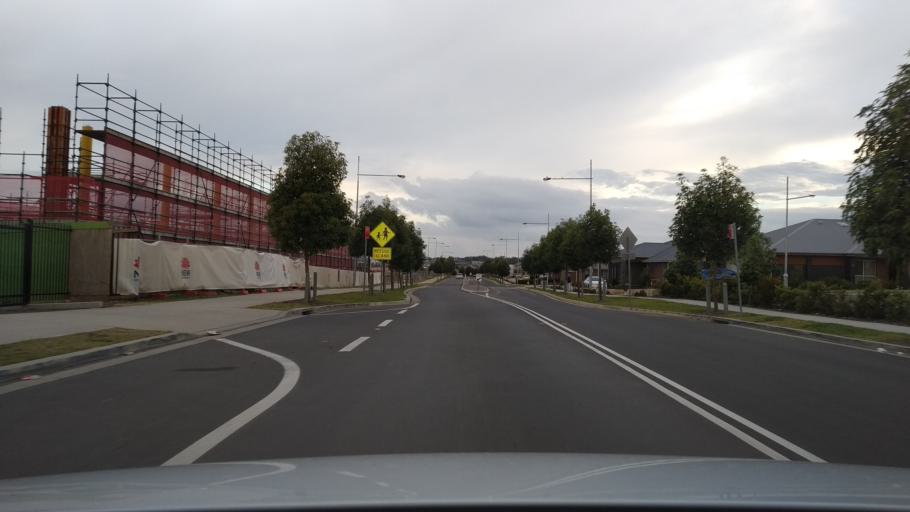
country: AU
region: New South Wales
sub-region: Camden
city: Narellan
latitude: -33.9979
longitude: 150.7348
